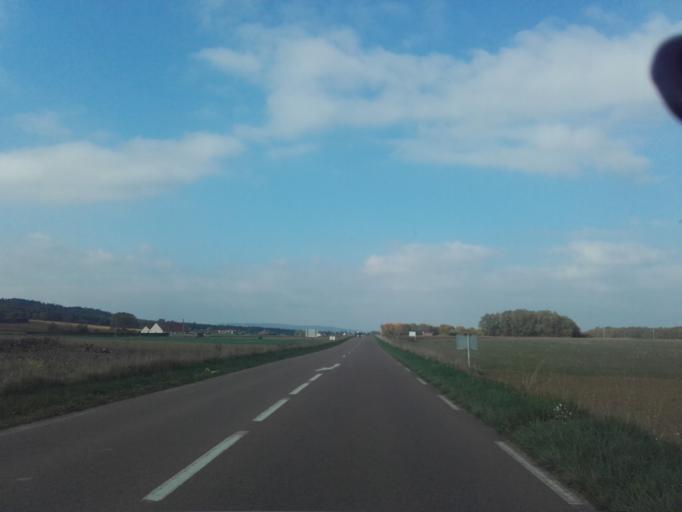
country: FR
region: Bourgogne
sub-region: Departement de Saone-et-Loire
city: Rully
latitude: 46.8818
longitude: 4.7523
